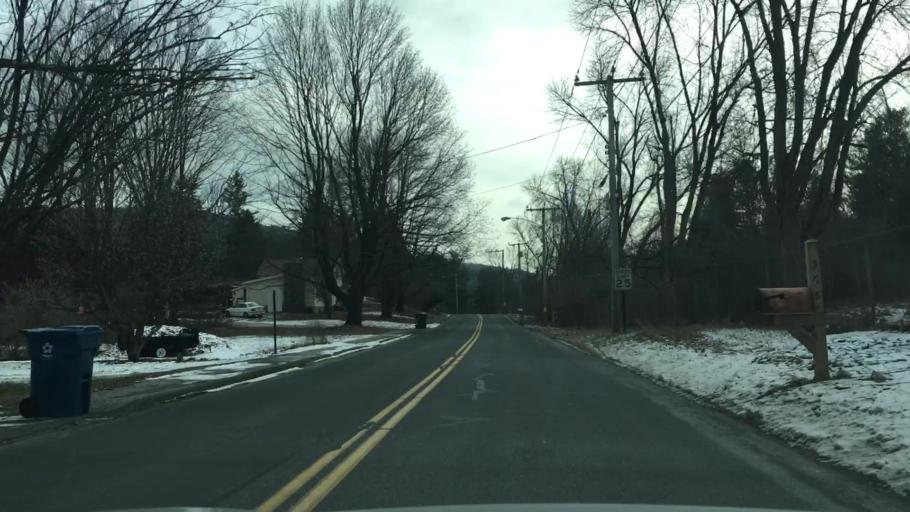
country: US
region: Massachusetts
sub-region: Berkshire County
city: Lee
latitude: 42.2947
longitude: -73.2471
